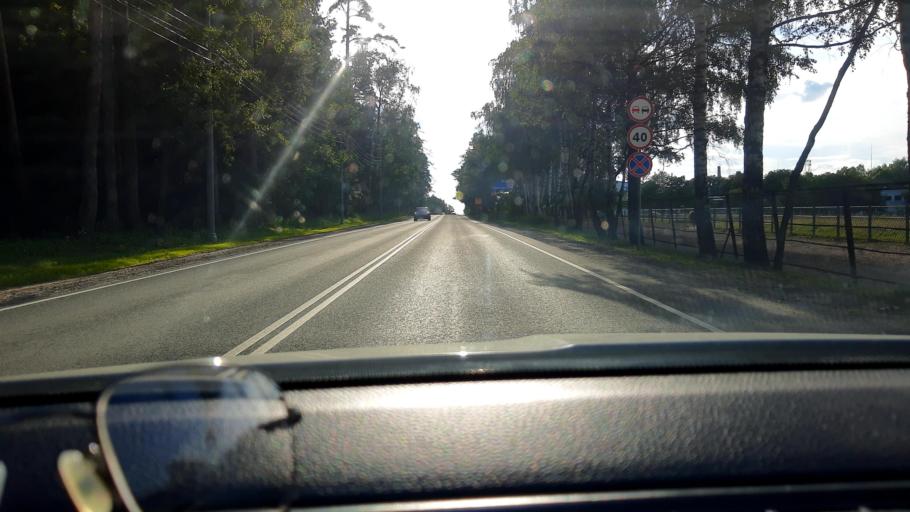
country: RU
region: Moskovskaya
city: Nikolina Gora
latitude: 55.7066
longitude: 37.0329
